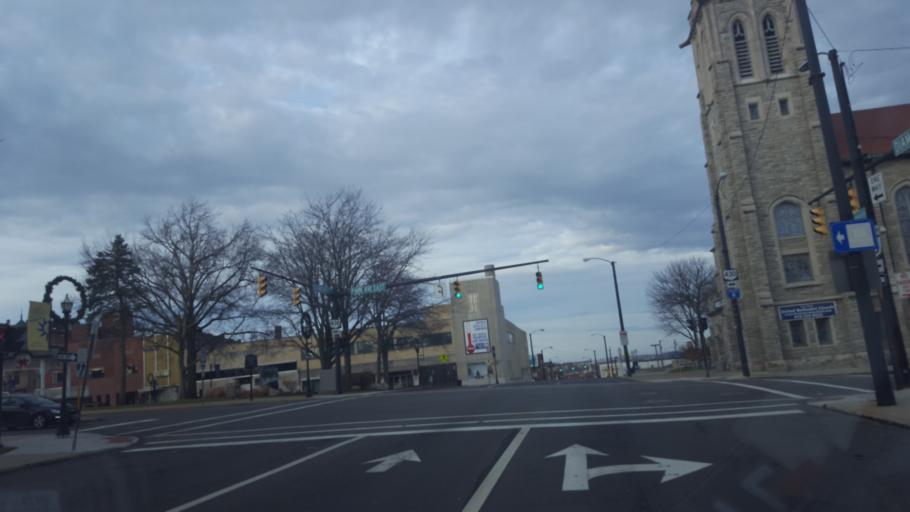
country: US
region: Ohio
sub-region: Richland County
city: Mansfield
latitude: 40.7582
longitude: -82.5141
